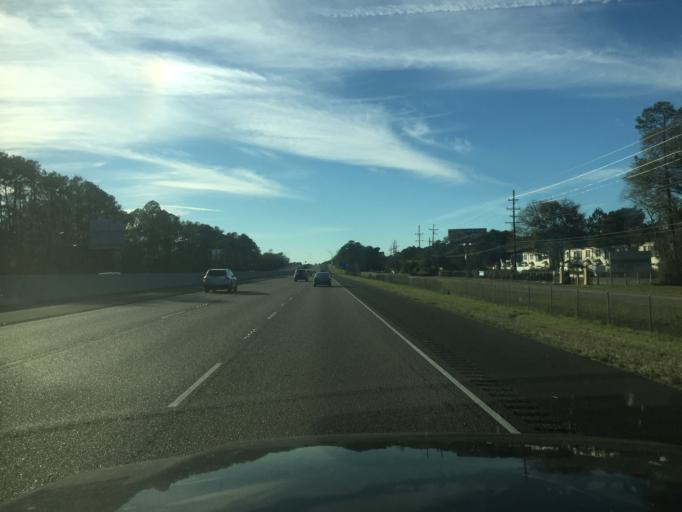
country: US
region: Louisiana
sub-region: Saint Tammany Parish
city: Slidell
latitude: 30.3103
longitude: -89.7620
